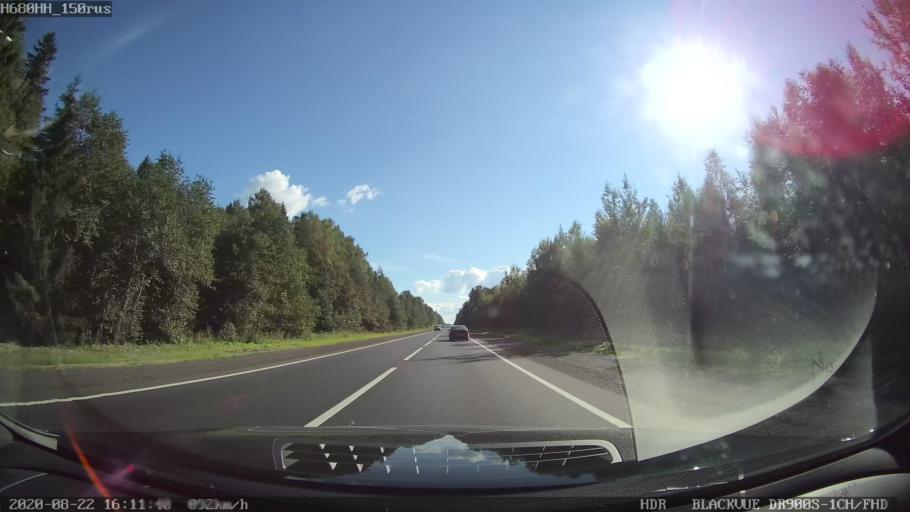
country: RU
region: Tverskaya
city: Rameshki
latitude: 57.4988
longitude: 36.2578
